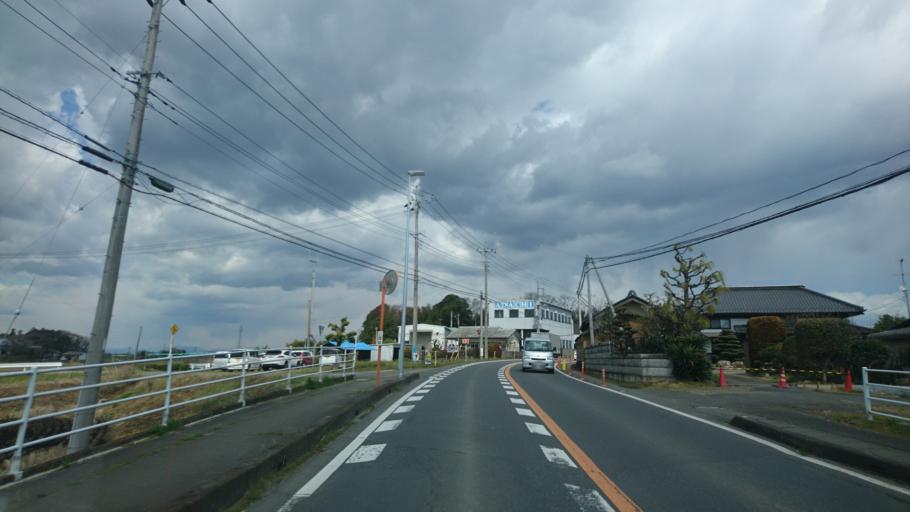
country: JP
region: Ibaraki
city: Yuki
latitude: 36.2282
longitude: 139.9317
